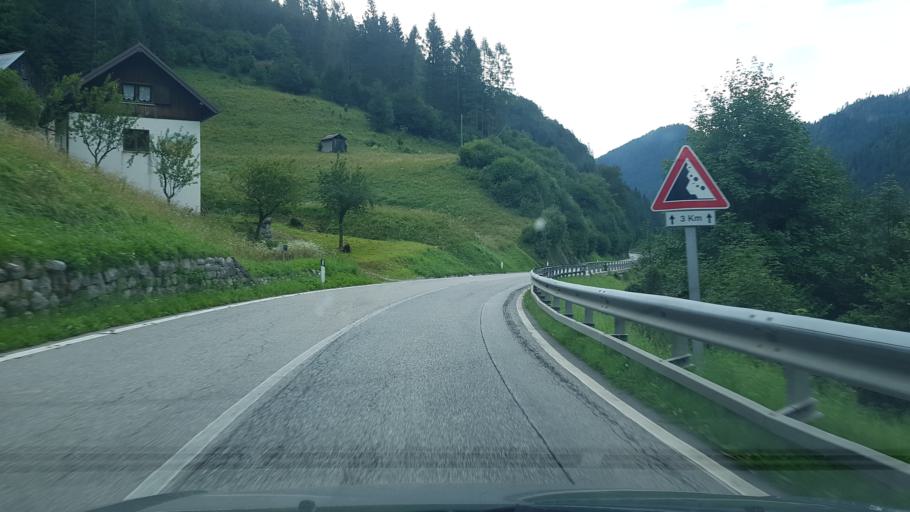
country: IT
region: Friuli Venezia Giulia
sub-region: Provincia di Udine
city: Forni Avoltri
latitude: 46.5813
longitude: 12.7854
